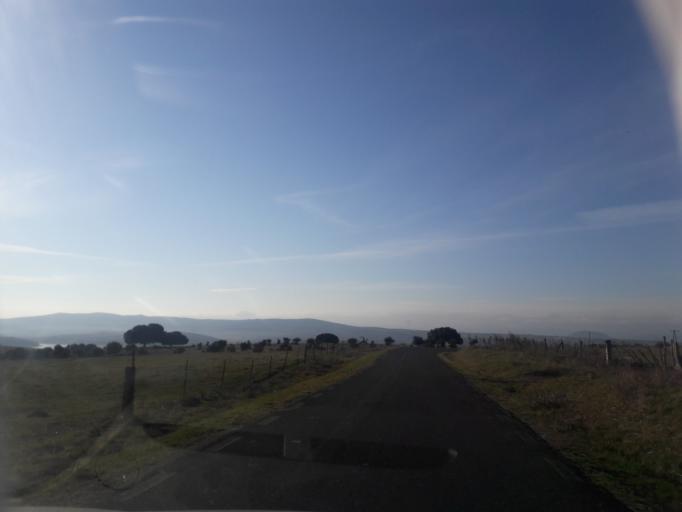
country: ES
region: Castille and Leon
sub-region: Provincia de Salamanca
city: Salvatierra de Tormes
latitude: 40.6094
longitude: -5.6021
